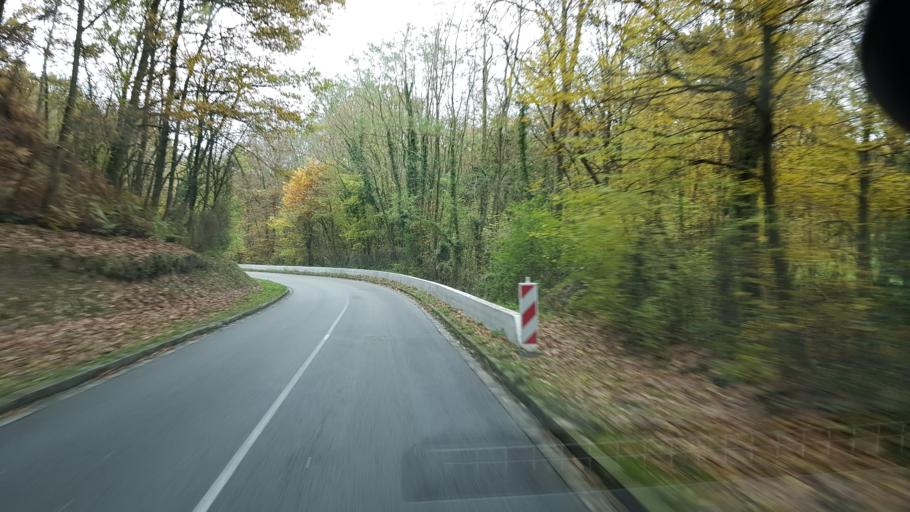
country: FR
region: Ile-de-France
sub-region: Departement des Yvelines
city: Chevreuse
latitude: 48.7153
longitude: 2.0208
